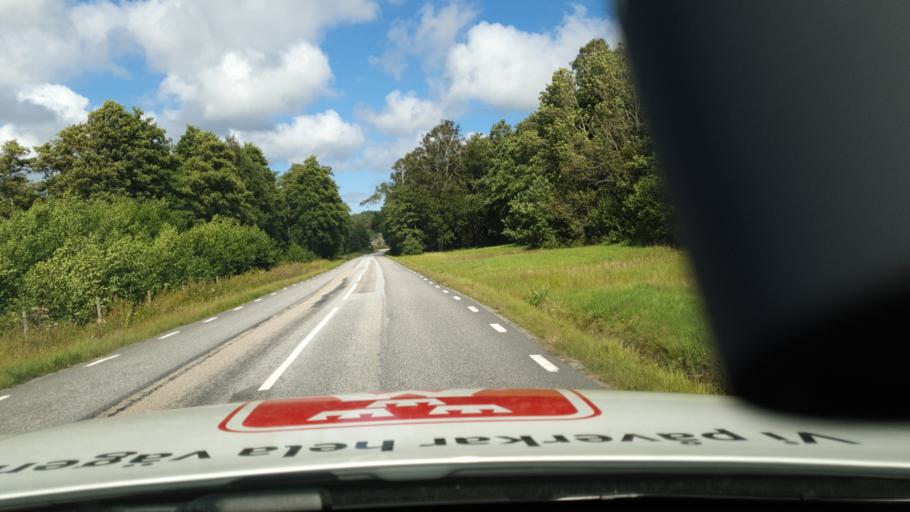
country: SE
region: Vaestra Goetaland
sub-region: Lysekils Kommun
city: Lysekil
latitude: 58.1965
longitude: 11.5310
